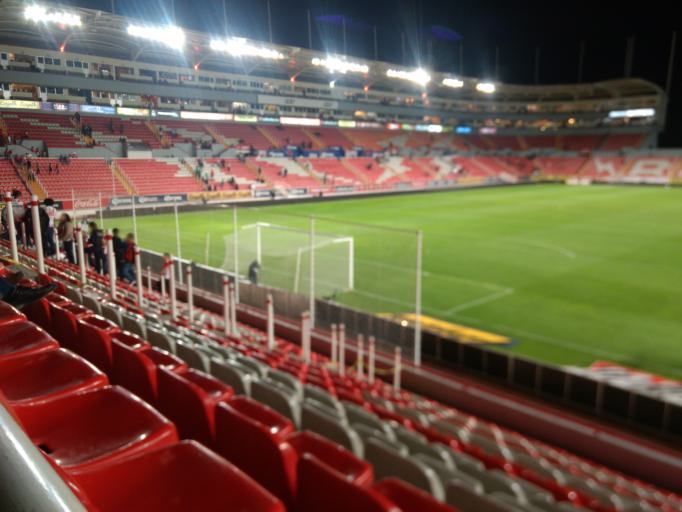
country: MX
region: Aguascalientes
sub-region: Aguascalientes
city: Aguascalientes
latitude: 21.8813
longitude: -102.2753
